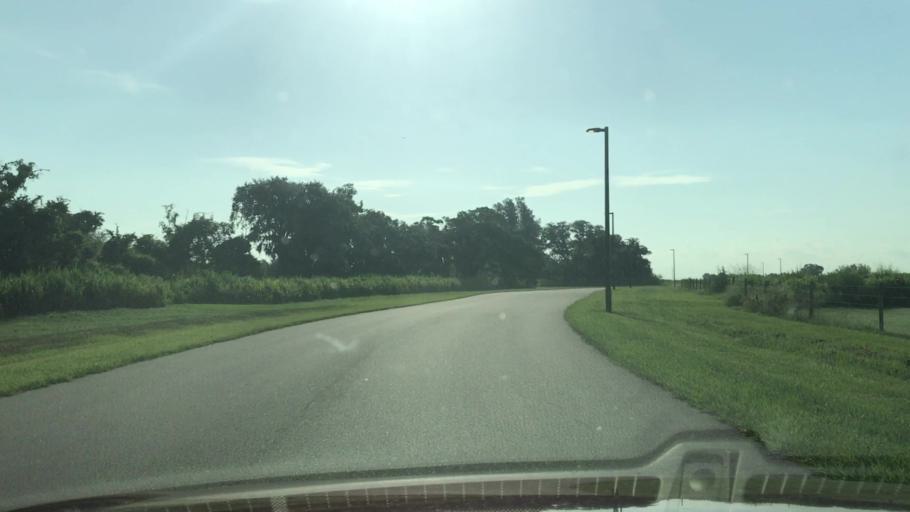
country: US
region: Florida
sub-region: Sarasota County
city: The Meadows
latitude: 27.4716
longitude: -82.3939
